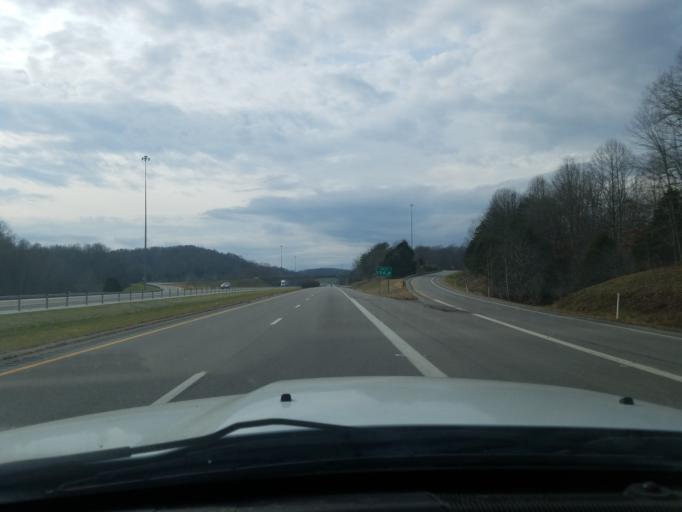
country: US
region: Kentucky
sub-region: Carter County
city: Olive Hill
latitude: 38.3323
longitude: -83.2048
